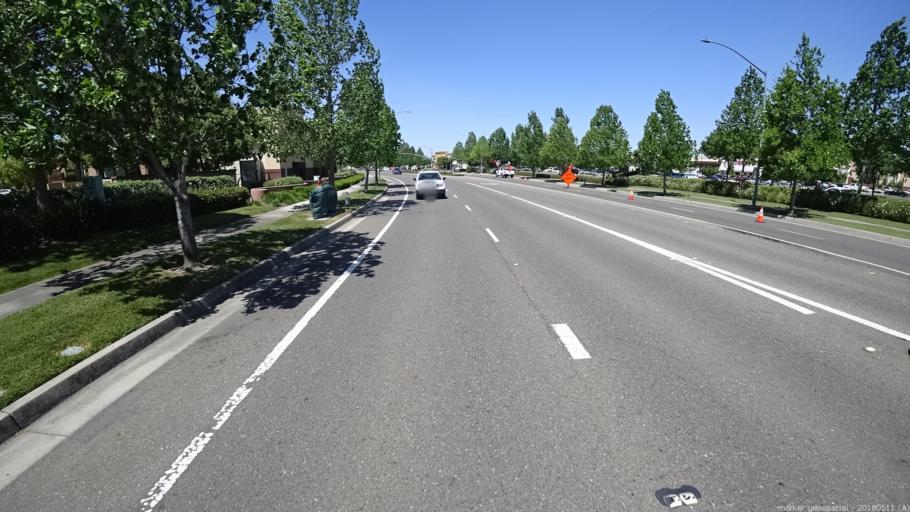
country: US
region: California
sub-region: Sacramento County
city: Sacramento
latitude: 38.6396
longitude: -121.4983
